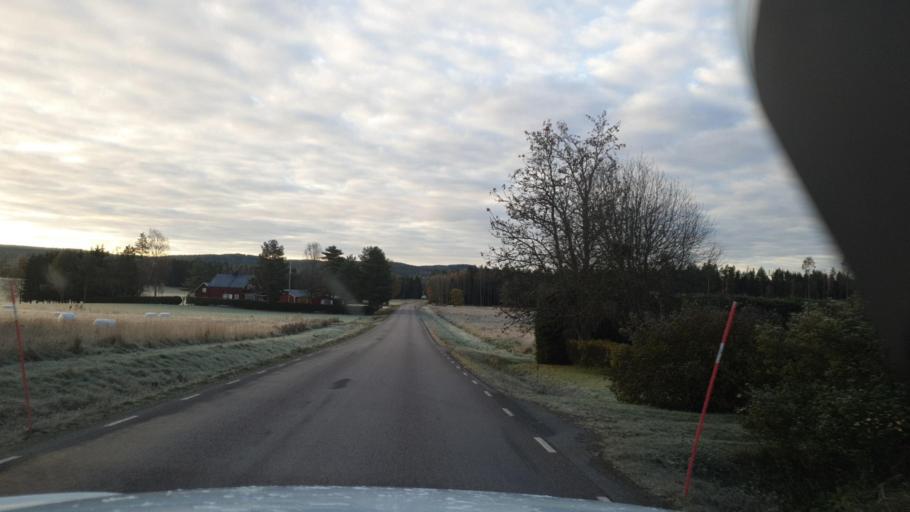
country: SE
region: Vaermland
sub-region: Eda Kommun
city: Charlottenberg
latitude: 59.7416
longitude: 12.1676
